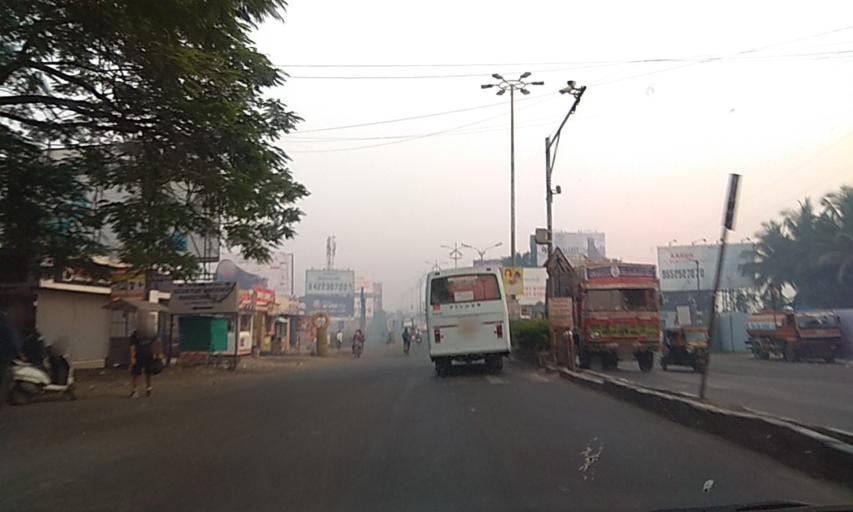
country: IN
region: Maharashtra
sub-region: Pune Division
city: Lohogaon
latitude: 18.5235
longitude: 73.9322
